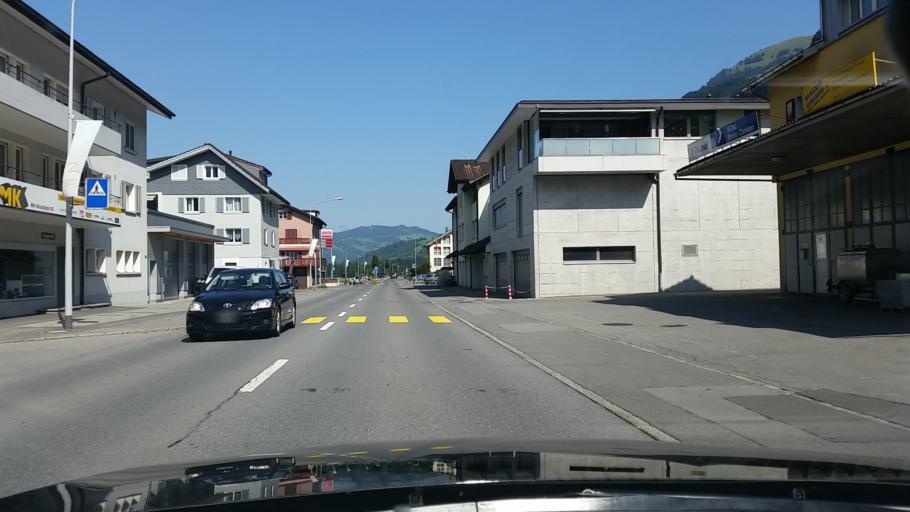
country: CH
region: Nidwalden
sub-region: Nidwalden
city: Wolfenschiessen
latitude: 46.9097
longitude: 8.3957
